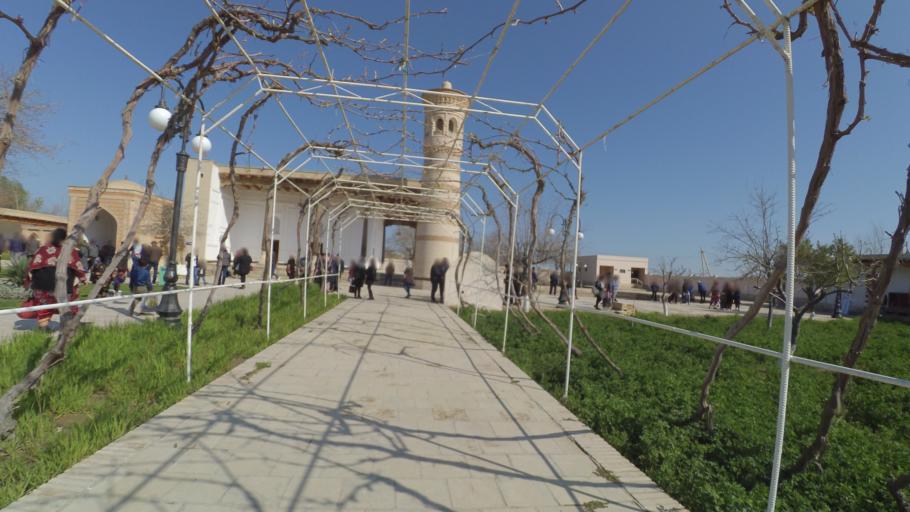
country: UZ
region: Bukhara
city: Kogon
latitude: 39.8051
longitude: 64.5403
